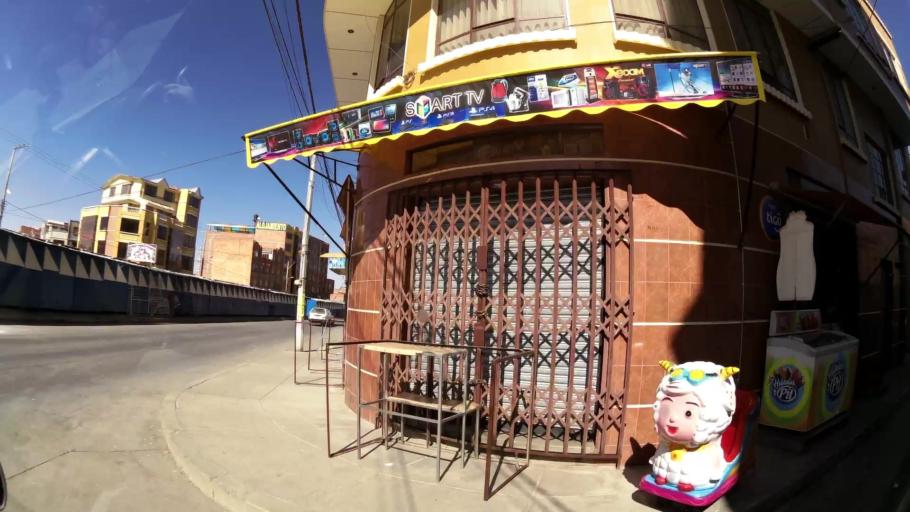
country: BO
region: La Paz
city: La Paz
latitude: -16.5144
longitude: -68.1614
